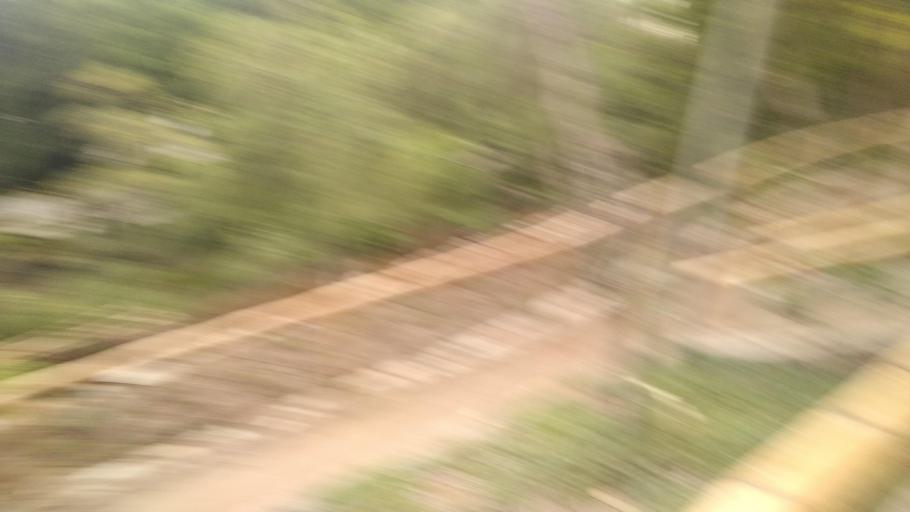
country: PE
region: Lima
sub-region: Lima
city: Surco
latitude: -12.1369
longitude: -76.9865
